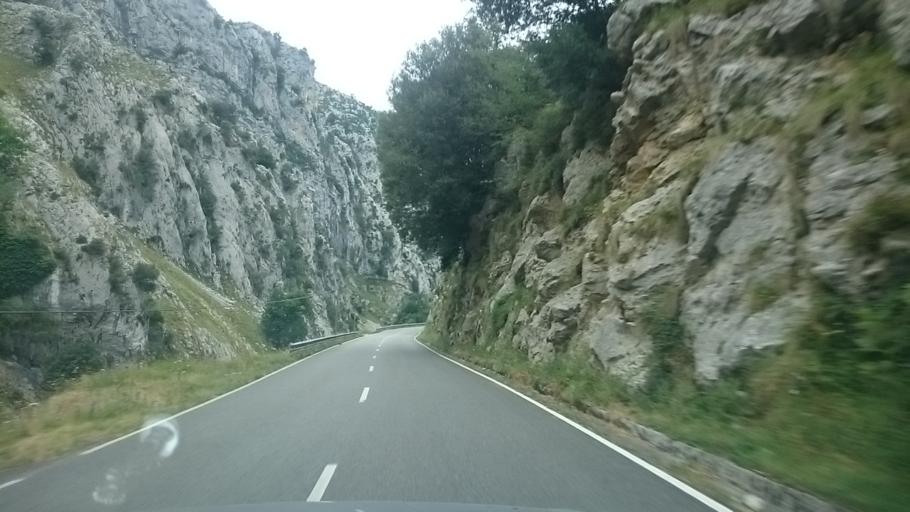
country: ES
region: Asturias
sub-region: Province of Asturias
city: Carrena
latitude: 43.2818
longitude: -4.8340
